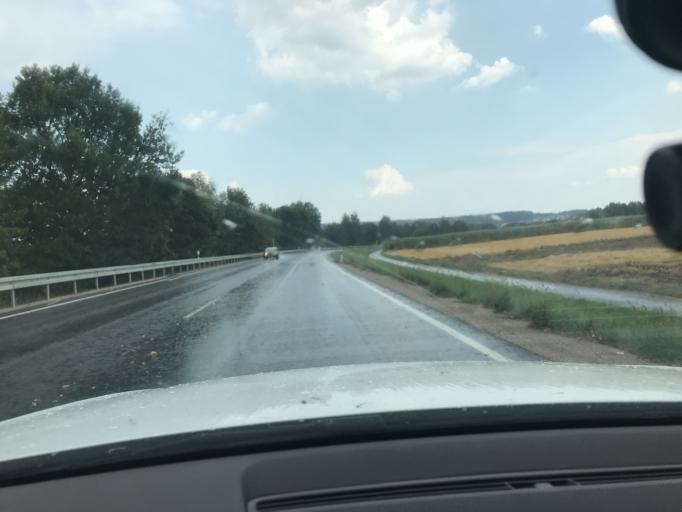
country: DE
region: Bavaria
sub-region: Upper Palatinate
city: Grafenwohr
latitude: 49.7328
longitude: 11.8952
